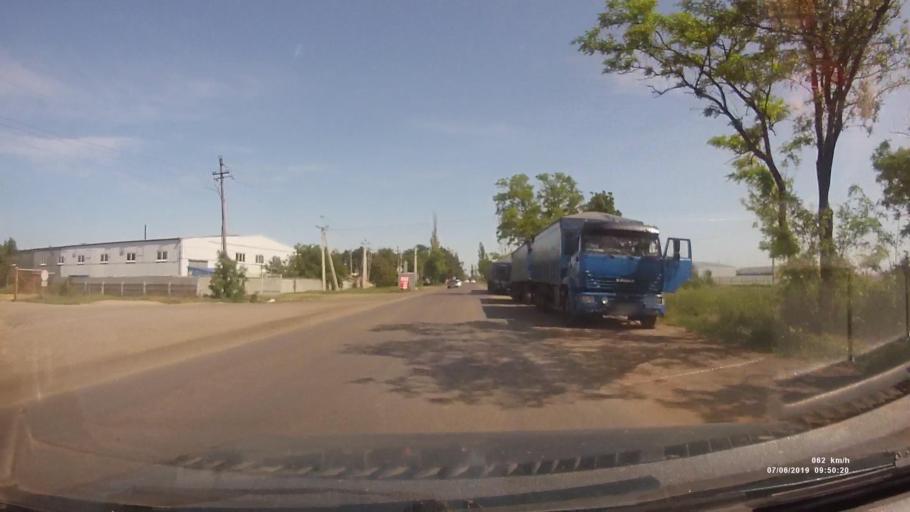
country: RU
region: Rostov
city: Azov
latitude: 47.0787
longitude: 39.4375
